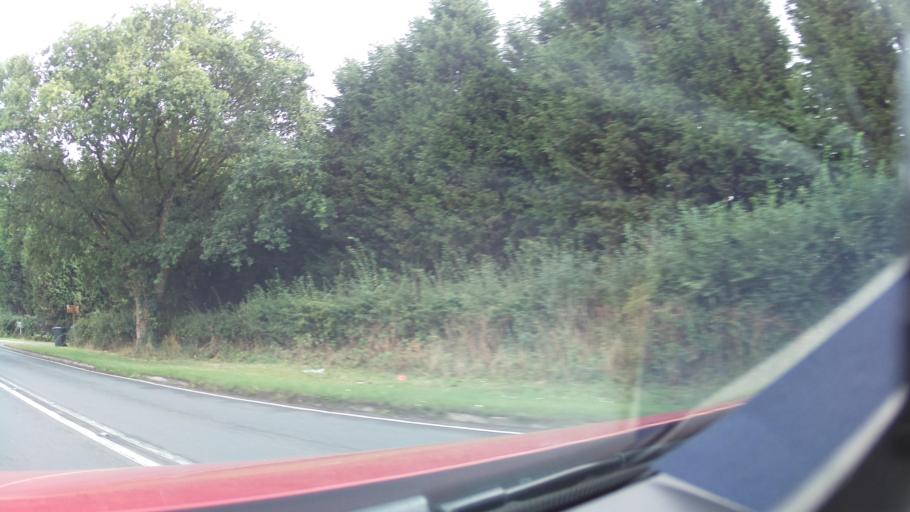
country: GB
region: England
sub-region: Worcestershire
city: Kidderminster
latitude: 52.3752
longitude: -2.2215
